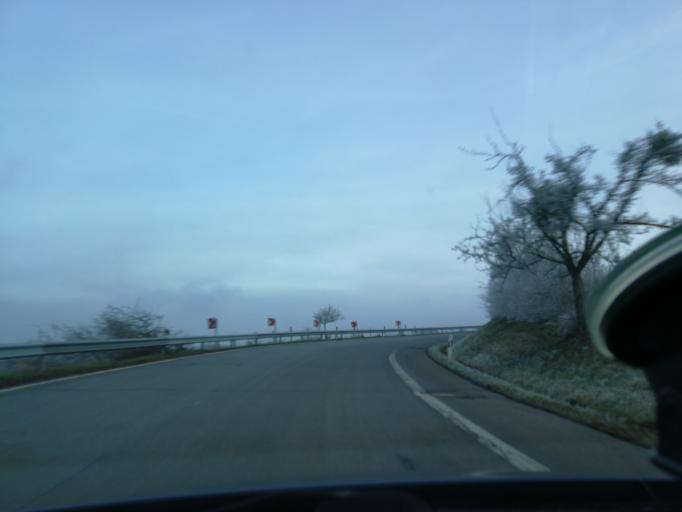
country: DE
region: Rheinland-Pfalz
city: Aach
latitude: 49.7781
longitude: 6.6101
